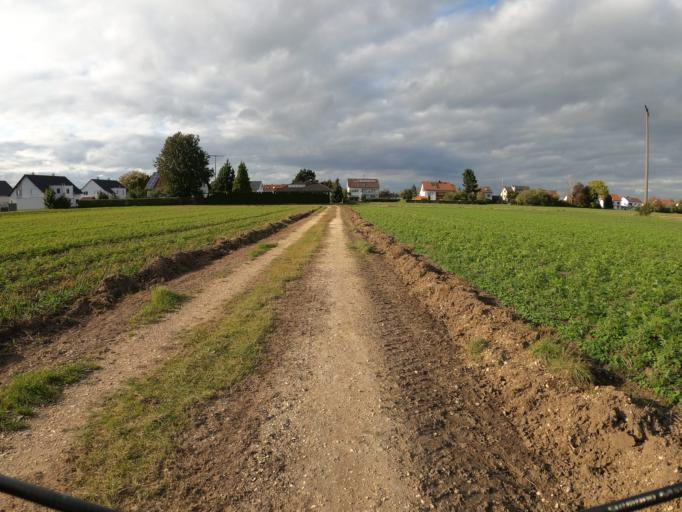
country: DE
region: Bavaria
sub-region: Swabia
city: Nersingen
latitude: 48.4219
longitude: 10.1210
